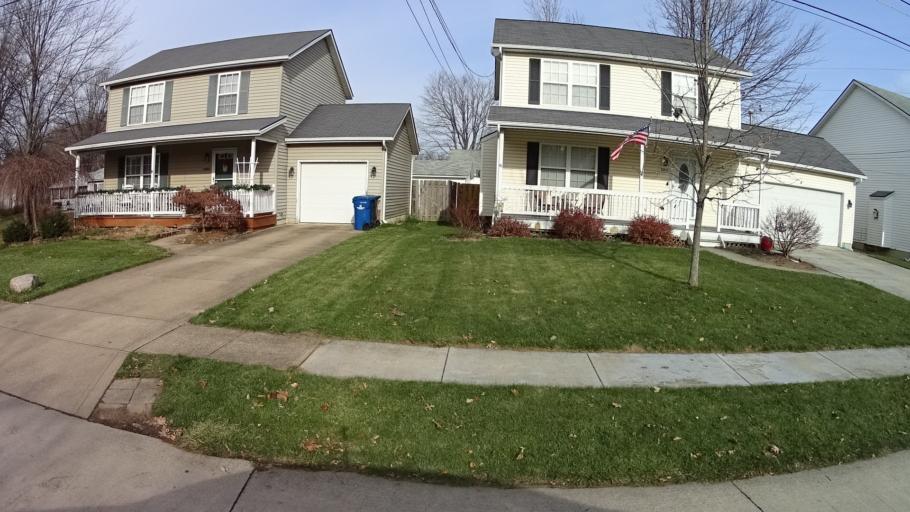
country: US
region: Ohio
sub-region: Lorain County
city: North Ridgeville
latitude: 41.3945
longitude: -81.9861
